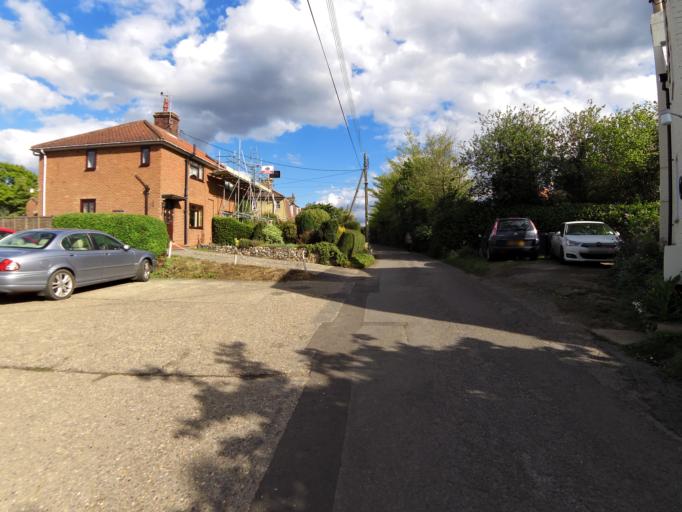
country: GB
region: England
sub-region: Suffolk
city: Woolpit
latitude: 52.2235
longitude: 0.8899
